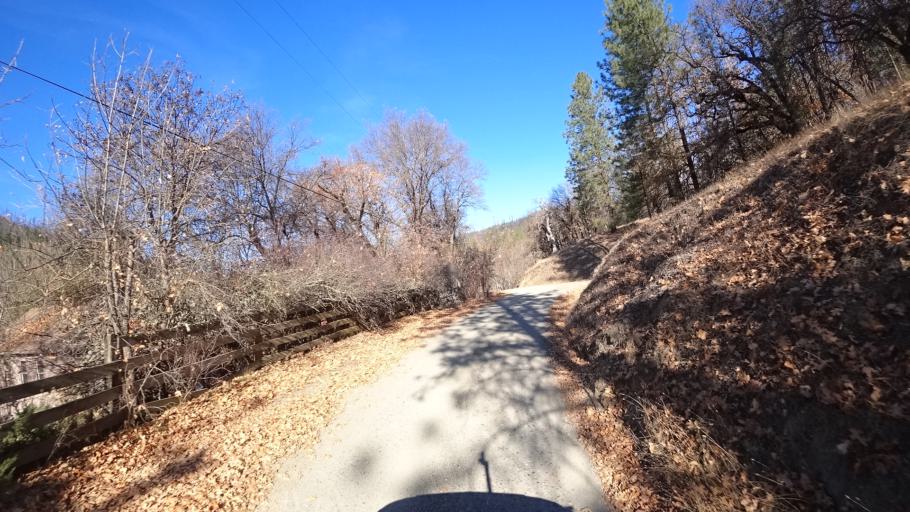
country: US
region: California
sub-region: Siskiyou County
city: Happy Camp
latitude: 41.8356
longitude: -123.0066
